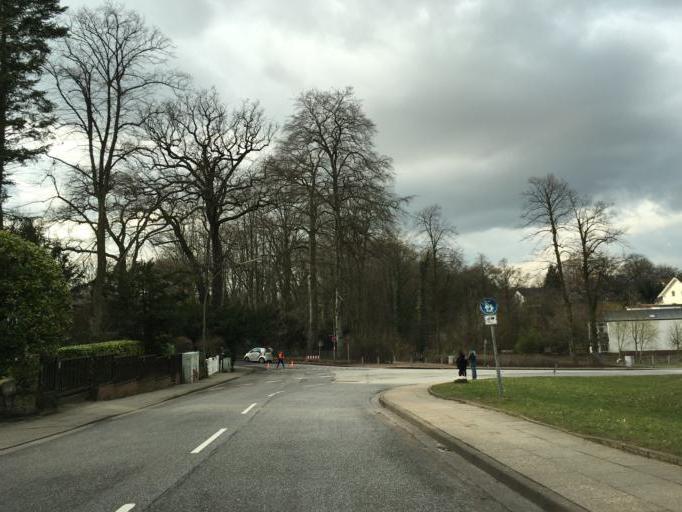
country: DE
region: Hamburg
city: Altona
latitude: 53.5541
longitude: 9.8742
